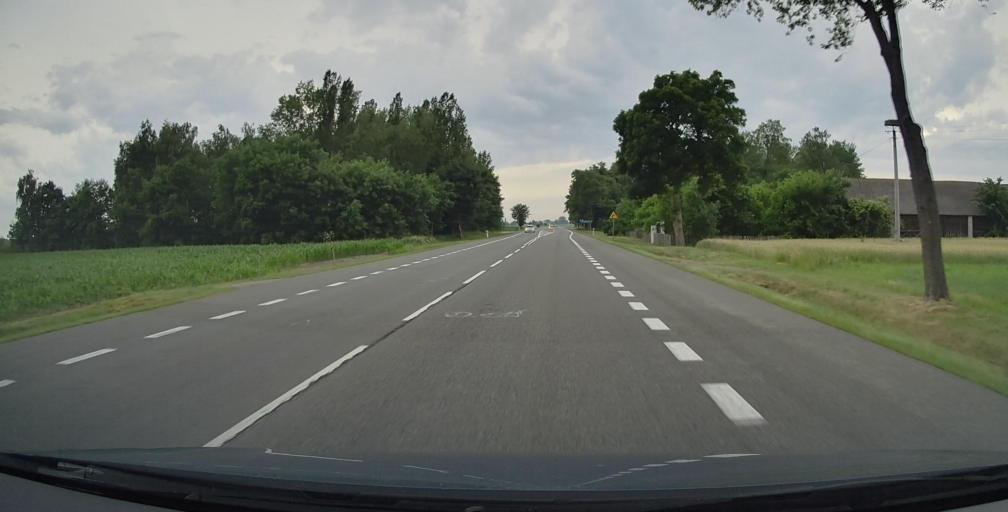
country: PL
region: Lublin Voivodeship
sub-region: Powiat lukowski
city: Trzebieszow
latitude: 52.0572
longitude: 22.5948
